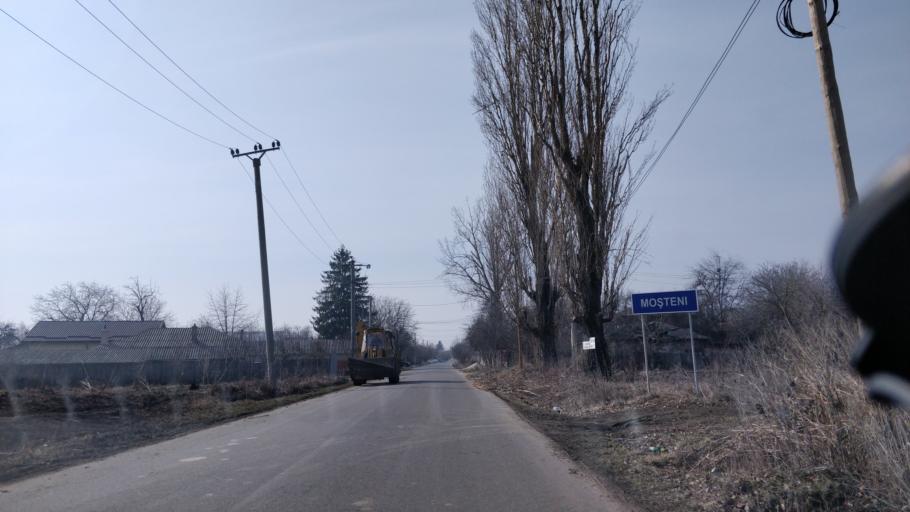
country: RO
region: Giurgiu
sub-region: Comuna Ulmi
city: Ulmi
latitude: 44.4632
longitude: 25.7894
